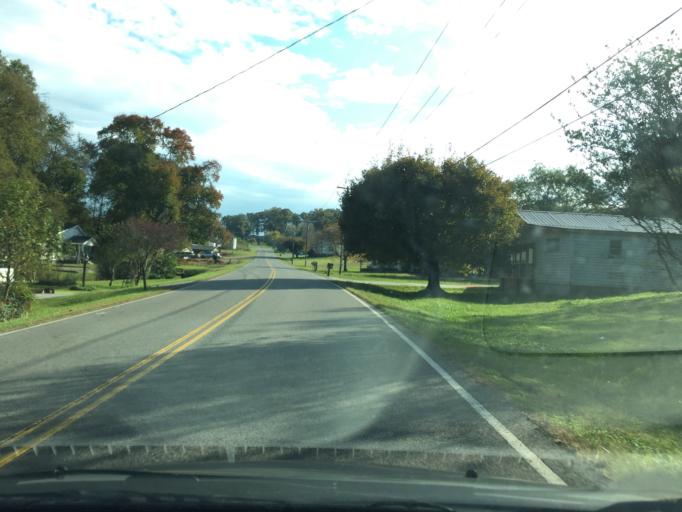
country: US
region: Tennessee
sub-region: Loudon County
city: Loudon
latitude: 35.6946
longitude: -84.3359
